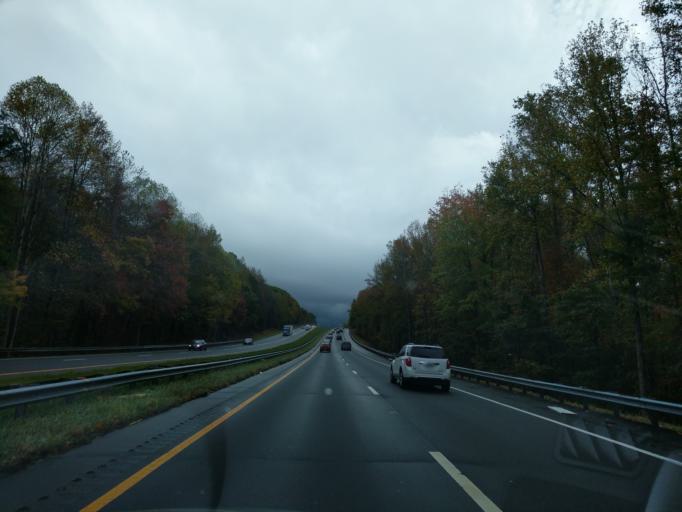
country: US
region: North Carolina
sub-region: Orange County
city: Hillsborough
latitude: 36.0491
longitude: -79.0538
